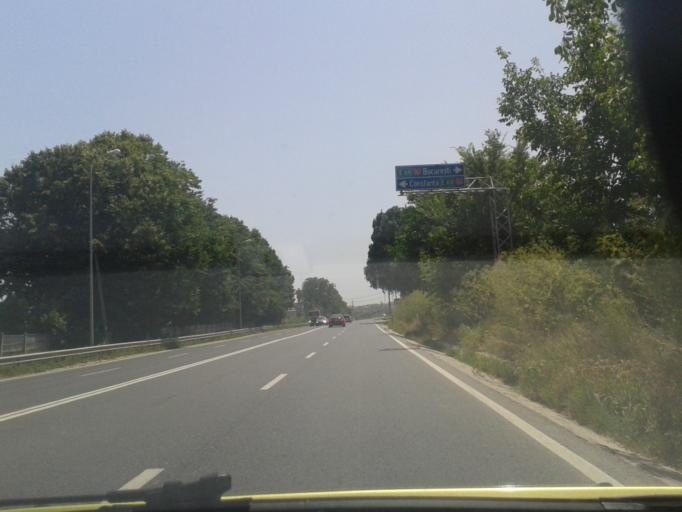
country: RO
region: Constanta
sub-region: Comuna Lumina
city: Lumina
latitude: 44.2770
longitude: 28.5574
